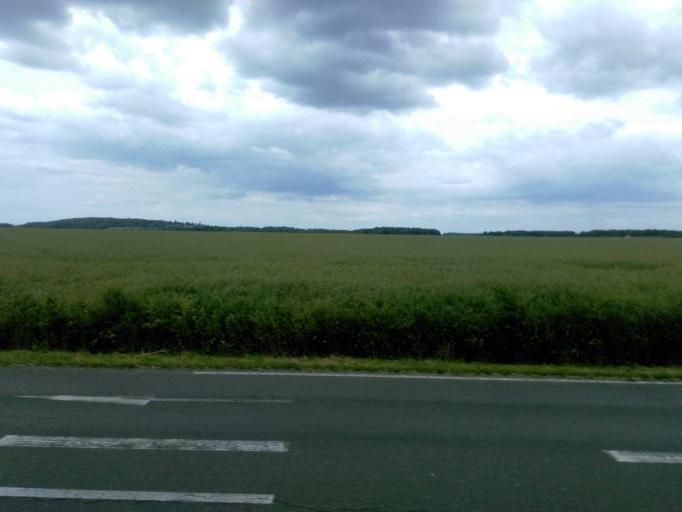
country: FR
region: Ile-de-France
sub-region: Departement du Val-d'Oise
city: Osny
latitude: 49.1013
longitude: 2.0424
